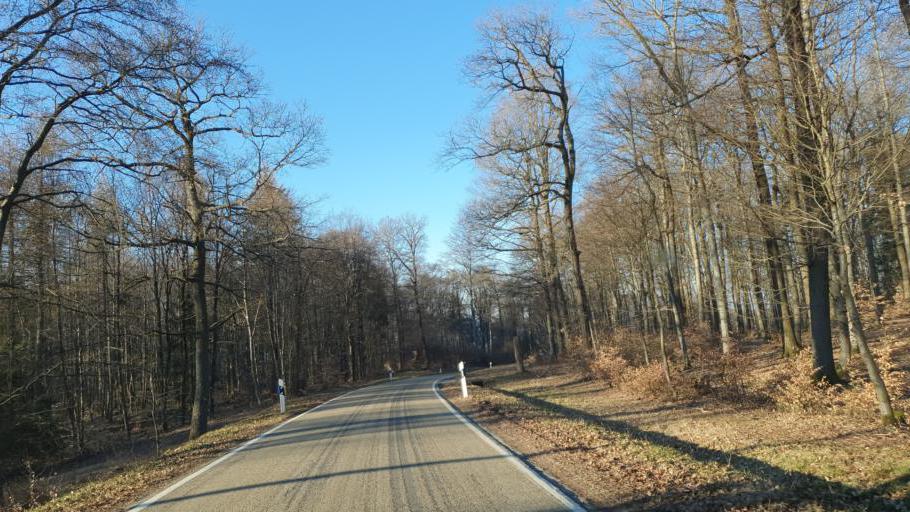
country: DE
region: Rheinland-Pfalz
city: Fockelberg
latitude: 49.5276
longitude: 7.4816
